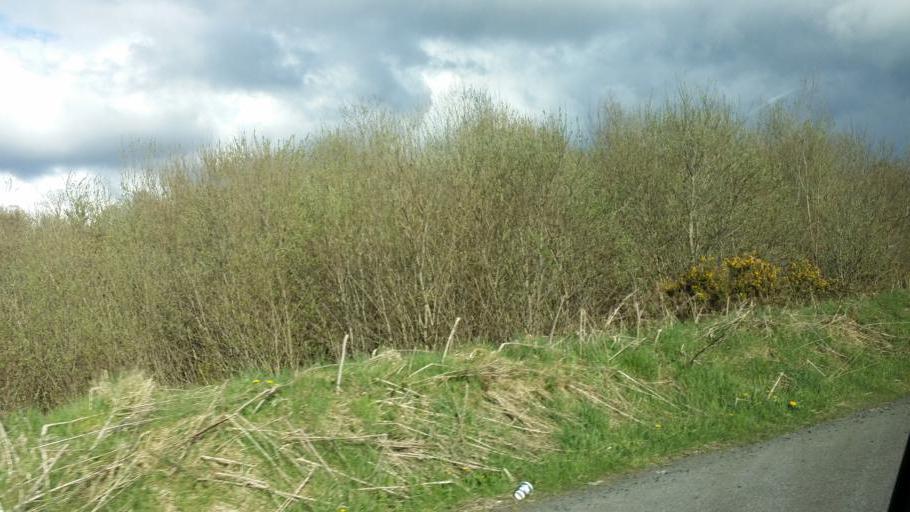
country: IE
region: Connaught
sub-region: County Leitrim
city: Manorhamilton
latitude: 54.3279
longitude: -8.2079
